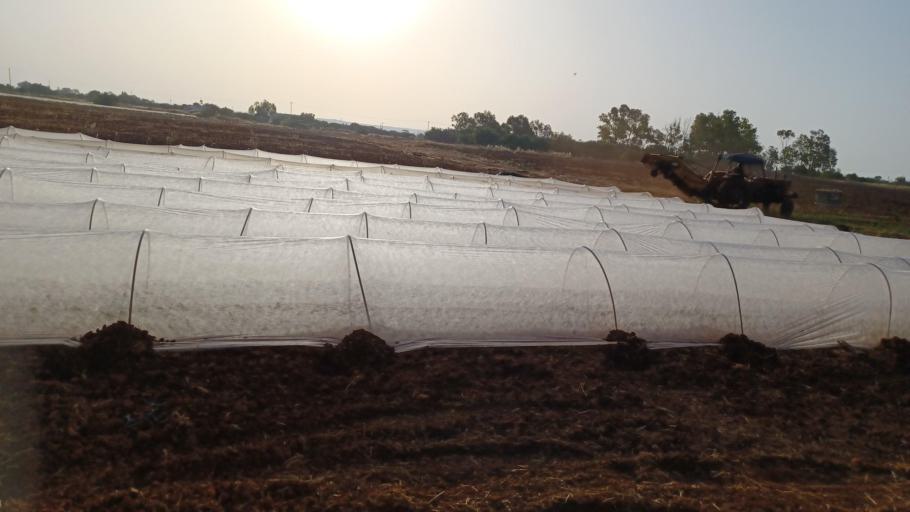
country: CY
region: Ammochostos
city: Liopetri
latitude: 34.9866
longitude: 33.8816
